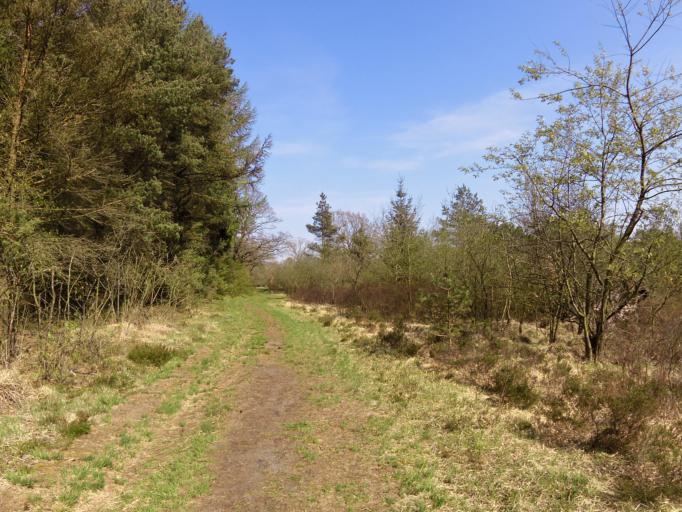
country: DK
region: South Denmark
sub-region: Tonder Kommune
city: Logumkloster
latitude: 55.1795
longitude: 8.9439
